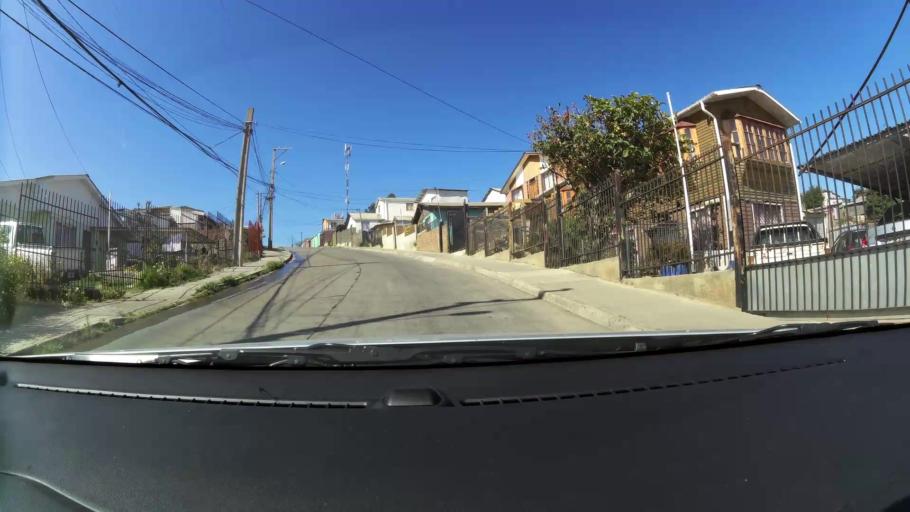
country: CL
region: Valparaiso
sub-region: Provincia de Valparaiso
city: Valparaiso
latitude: -33.0522
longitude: -71.6440
